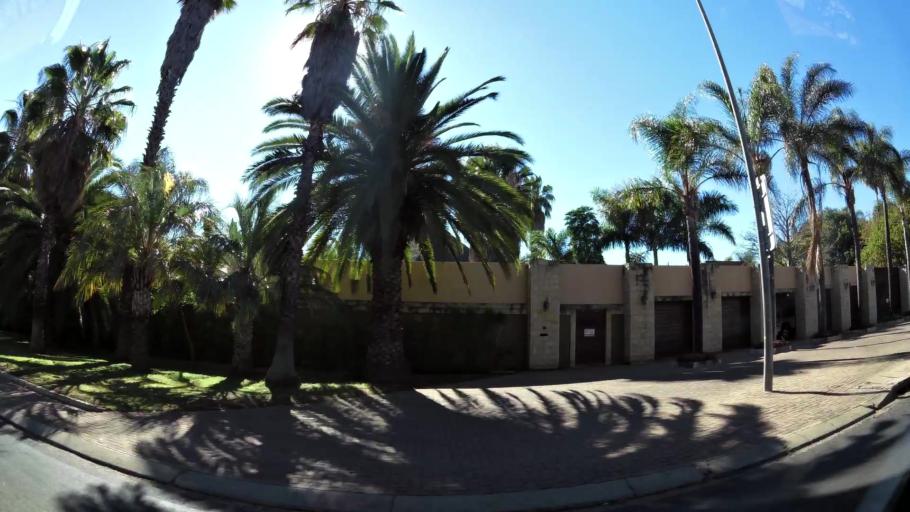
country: ZA
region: Limpopo
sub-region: Capricorn District Municipality
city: Polokwane
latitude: -23.8954
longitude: 29.4673
